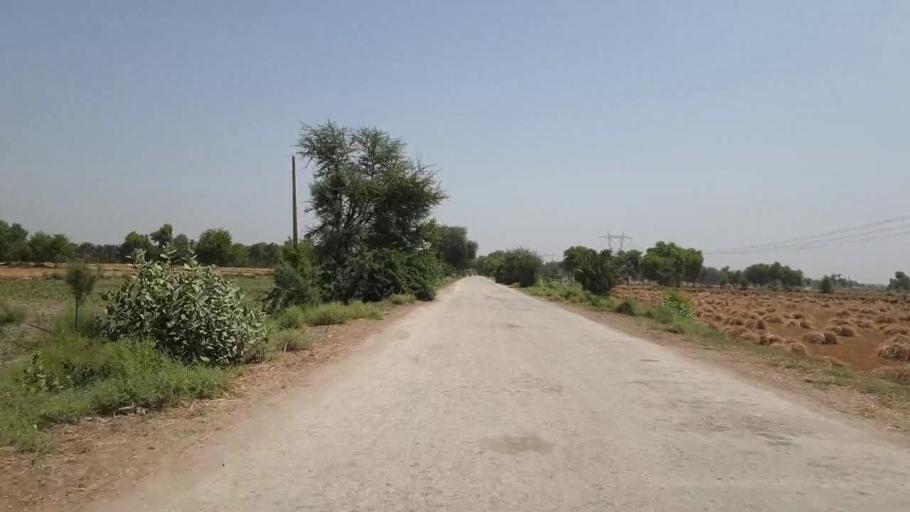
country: PK
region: Sindh
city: Adilpur
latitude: 27.8226
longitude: 69.2448
